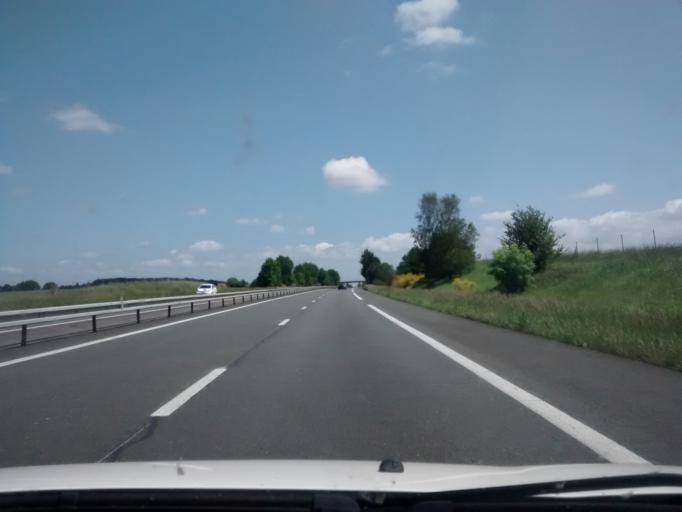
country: FR
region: Pays de la Loire
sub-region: Departement de la Sarthe
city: Trange
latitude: 48.0454
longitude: 0.1116
